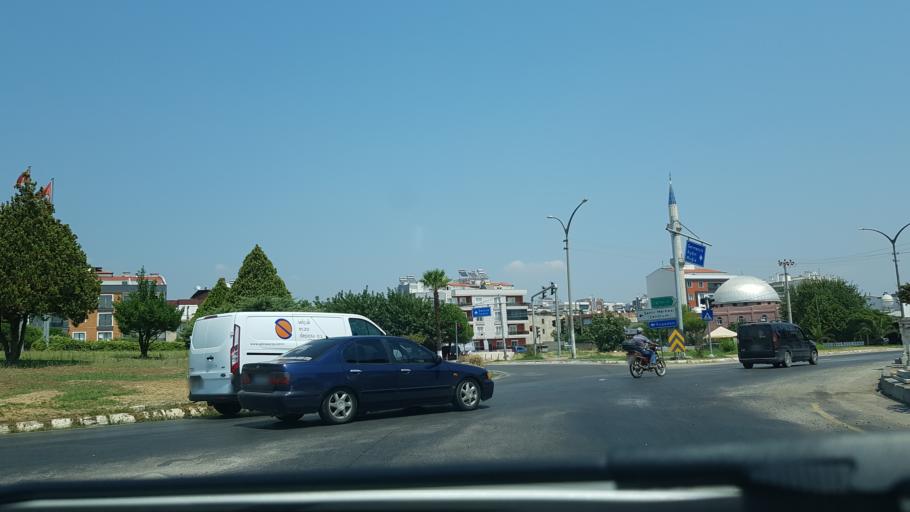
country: TR
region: Aydin
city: Ortaklar
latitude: 37.8831
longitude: 27.5054
